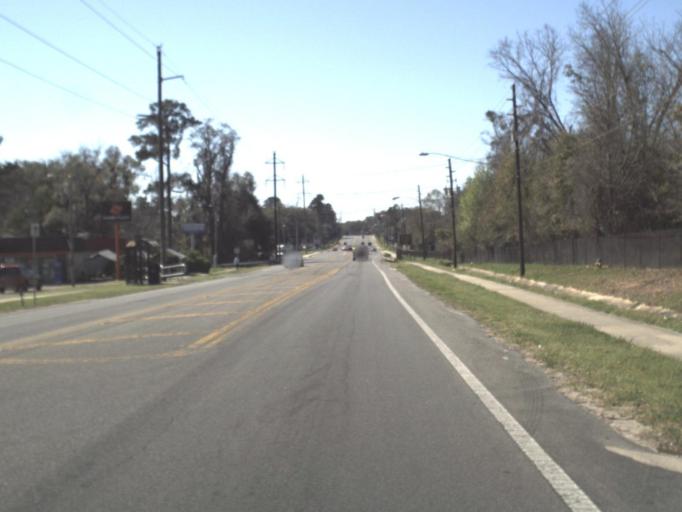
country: US
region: Florida
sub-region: Leon County
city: Tallahassee
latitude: 30.4157
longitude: -84.2827
